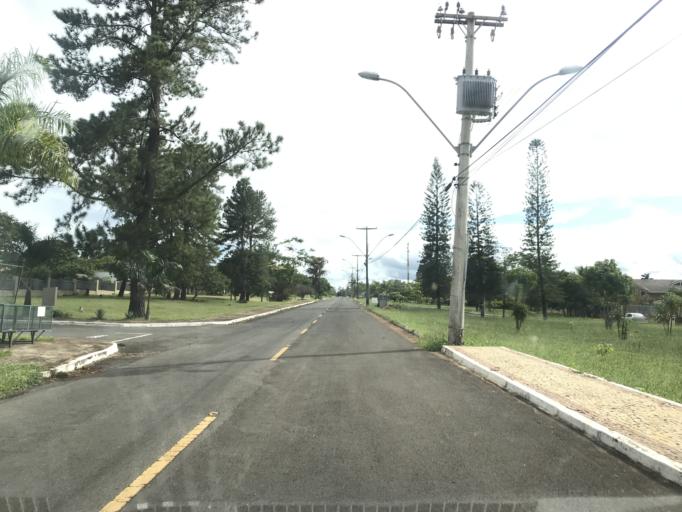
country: BR
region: Federal District
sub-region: Brasilia
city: Brasilia
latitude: -15.8942
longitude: -47.9190
